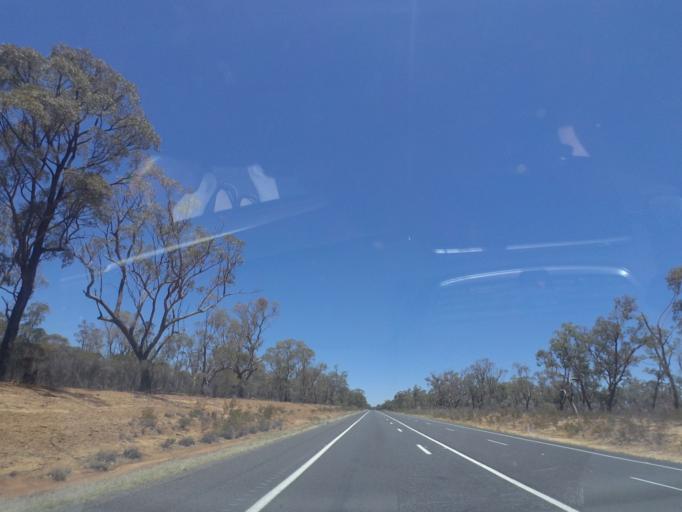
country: AU
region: New South Wales
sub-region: Warrumbungle Shire
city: Coonabarabran
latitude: -30.8718
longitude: 149.4499
